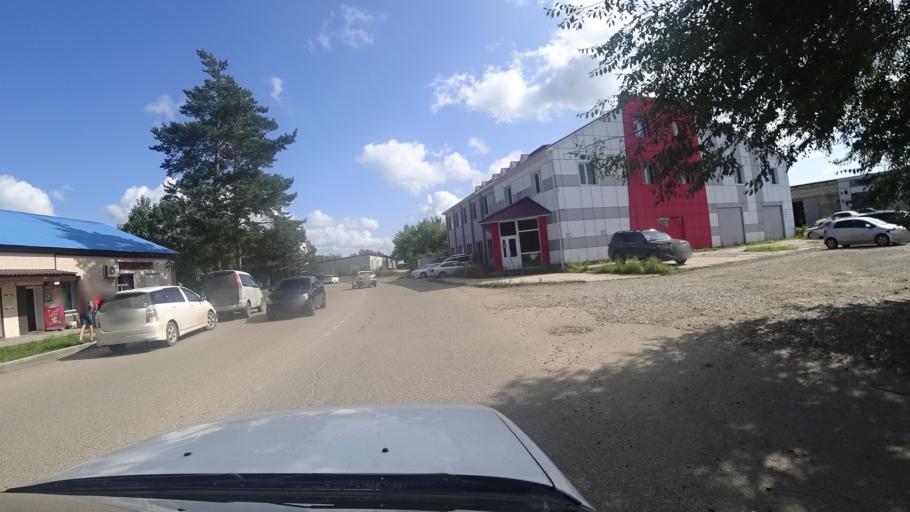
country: RU
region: Primorskiy
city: Dal'nerechensk
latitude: 45.9302
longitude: 133.7281
